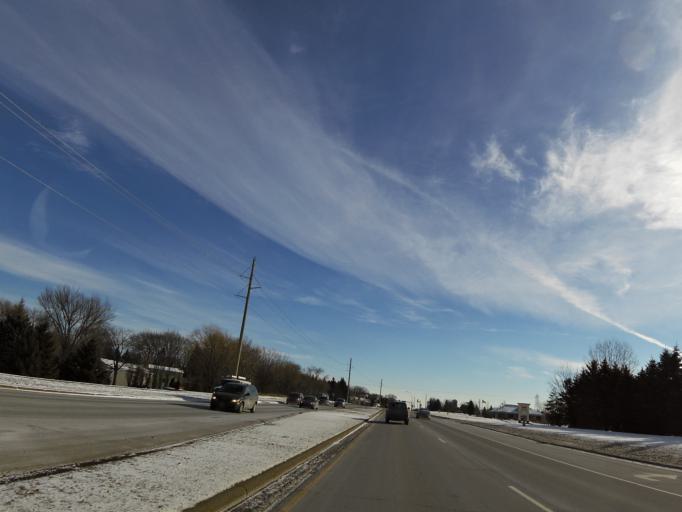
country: US
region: Minnesota
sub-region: Dakota County
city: Rosemount
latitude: 44.7318
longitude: -93.1602
